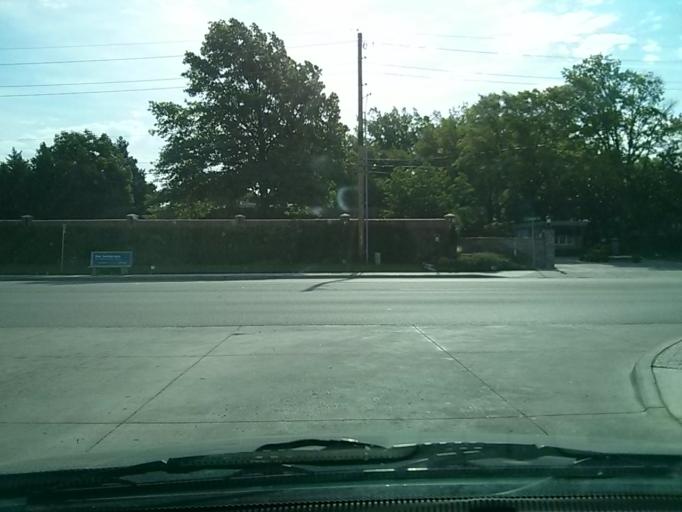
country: US
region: Oklahoma
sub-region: Tulsa County
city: Jenks
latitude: 36.0579
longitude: -95.9580
